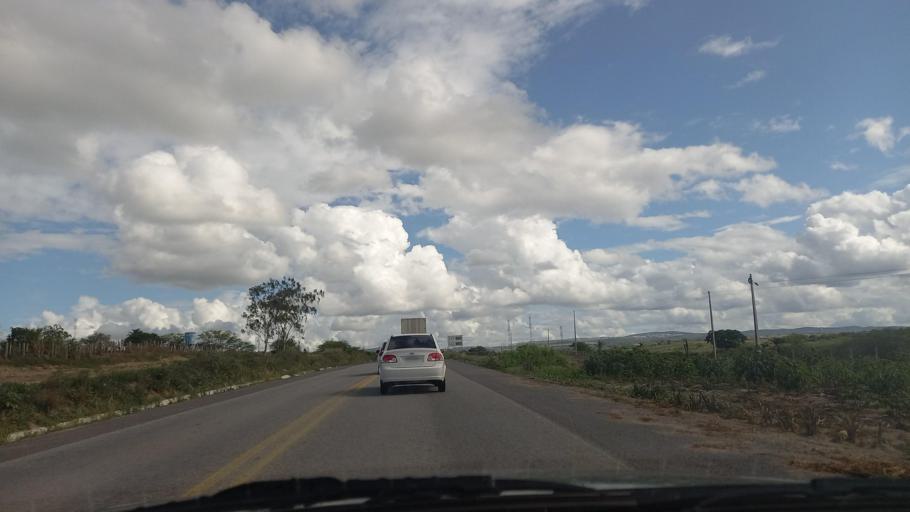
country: BR
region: Pernambuco
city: Garanhuns
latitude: -8.8019
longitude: -36.4398
